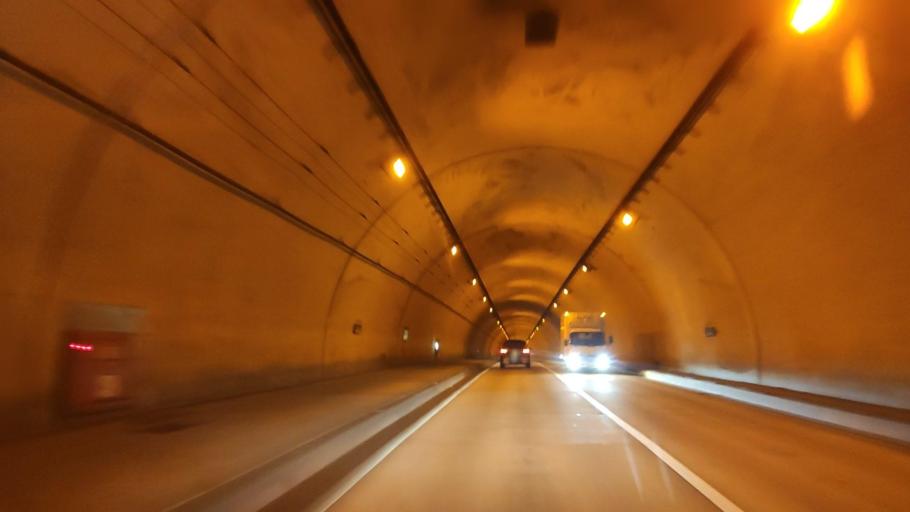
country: JP
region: Ehime
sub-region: Shikoku-chuo Shi
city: Matsuyama
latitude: 33.8822
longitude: 132.7103
